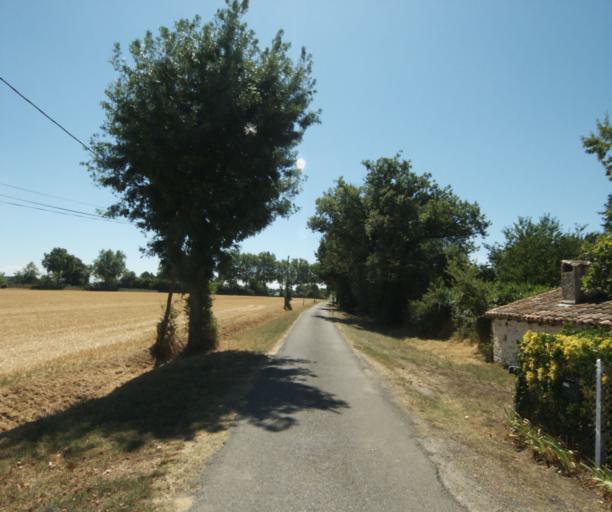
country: FR
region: Midi-Pyrenees
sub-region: Departement de la Haute-Garonne
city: Revel
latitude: 43.4733
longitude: 1.9519
